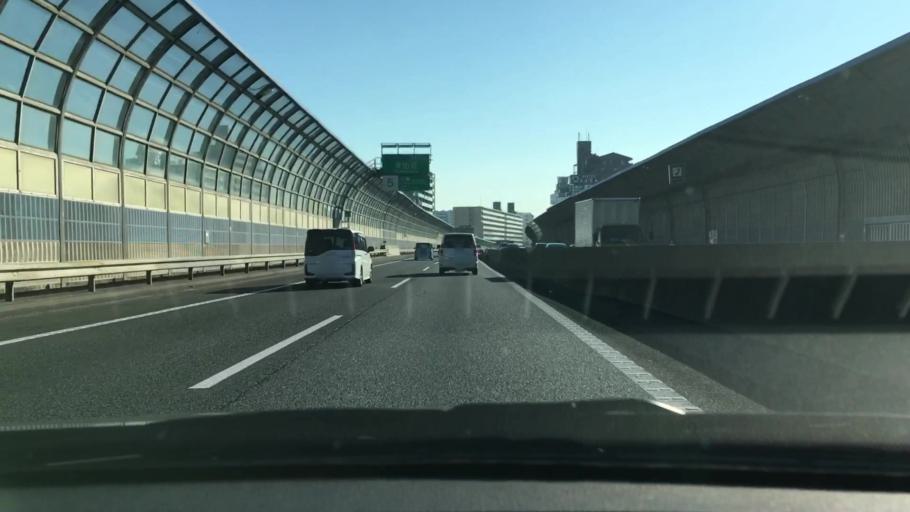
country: JP
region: Chiba
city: Funabashi
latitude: 35.6899
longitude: 139.9931
